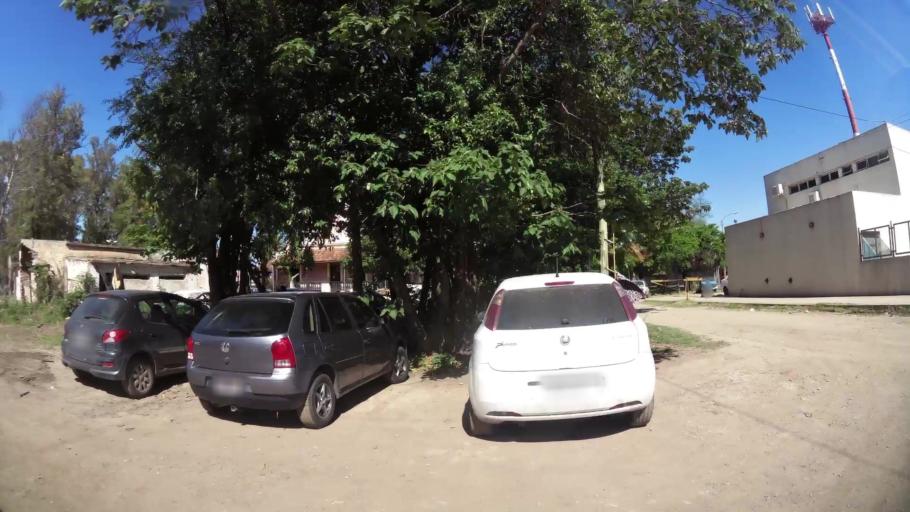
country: AR
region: Cordoba
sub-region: Departamento de Capital
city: Cordoba
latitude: -31.4425
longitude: -64.1430
